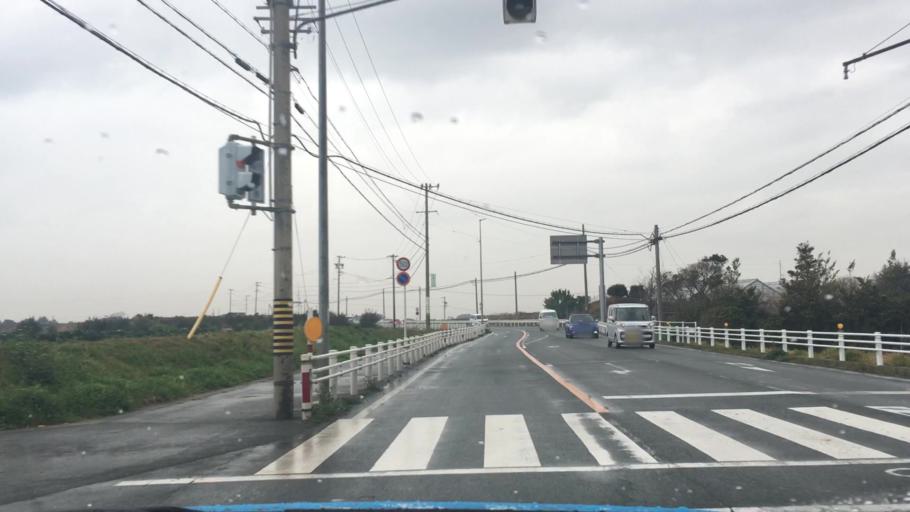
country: JP
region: Aichi
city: Toyohashi
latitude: 34.6653
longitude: 137.3770
